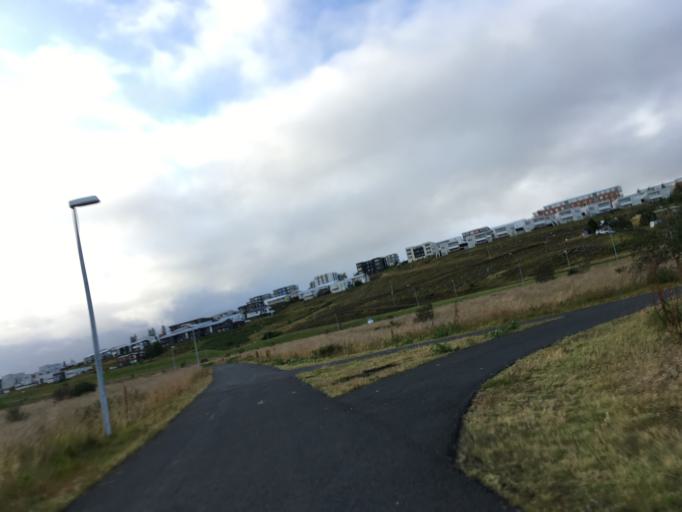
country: IS
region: Capital Region
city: Mosfellsbaer
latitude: 64.1318
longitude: -21.7587
